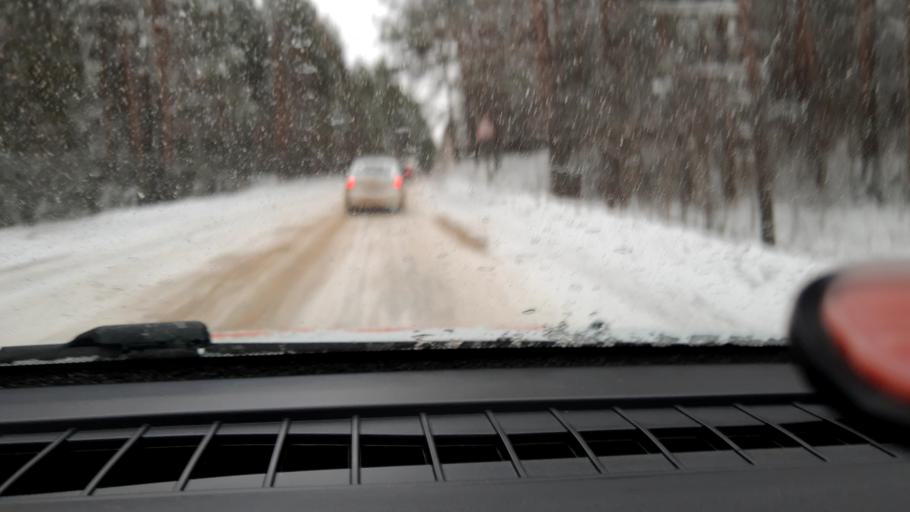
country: RU
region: Nizjnij Novgorod
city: Pamyat' Parizhskoy Kommuny
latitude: 56.2791
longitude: 44.3859
